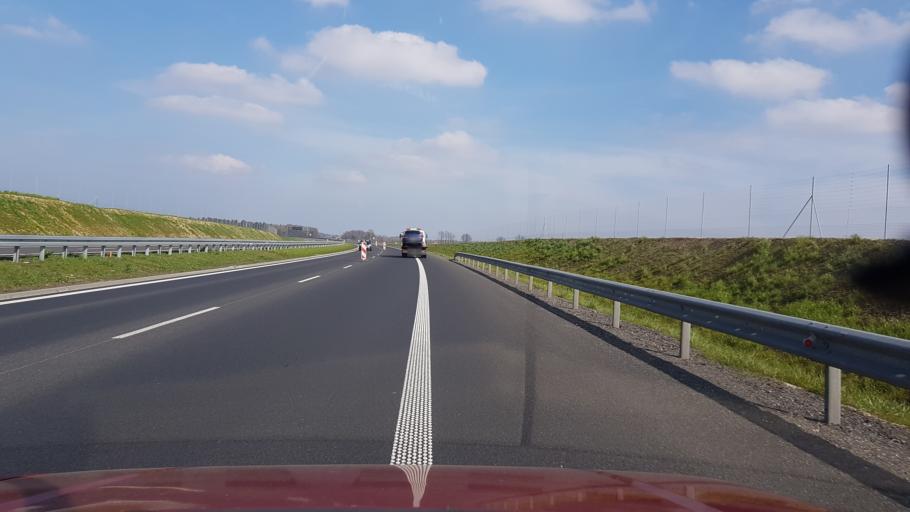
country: PL
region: West Pomeranian Voivodeship
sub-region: Powiat goleniowski
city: Osina
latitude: 53.6413
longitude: 15.0577
